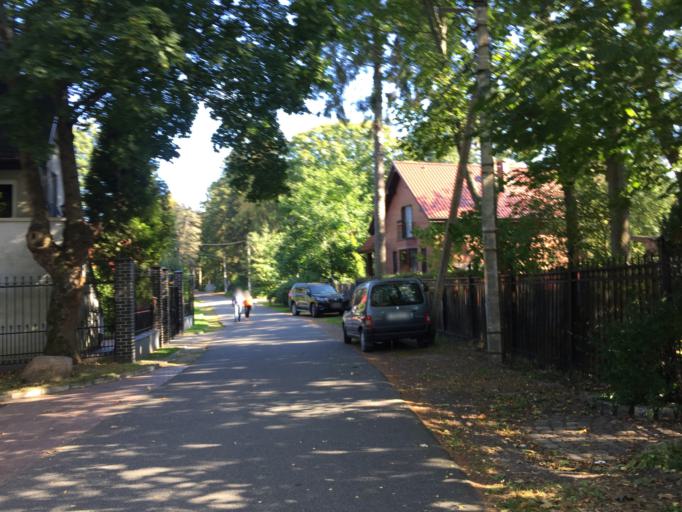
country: RU
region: Kaliningrad
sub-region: Gorod Svetlogorsk
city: Svetlogorsk
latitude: 54.9436
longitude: 20.1387
